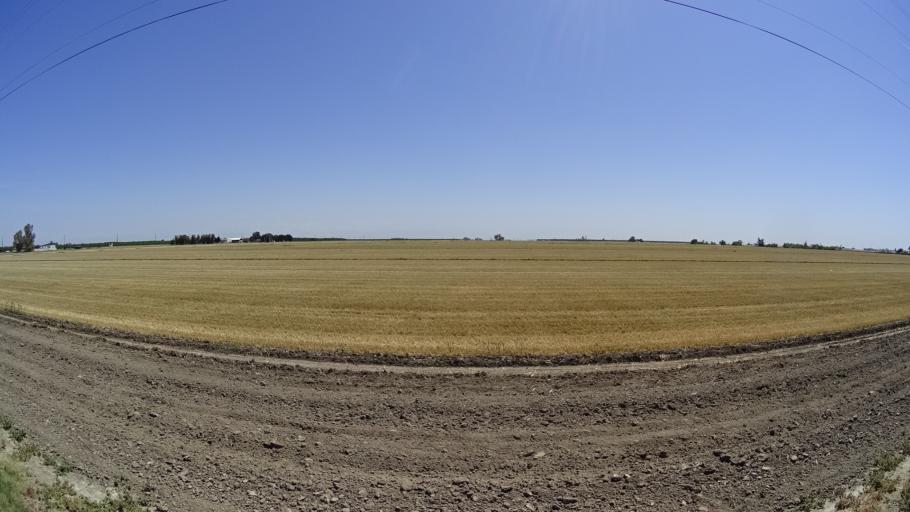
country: US
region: California
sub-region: Kings County
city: Armona
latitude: 36.2358
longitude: -119.7267
